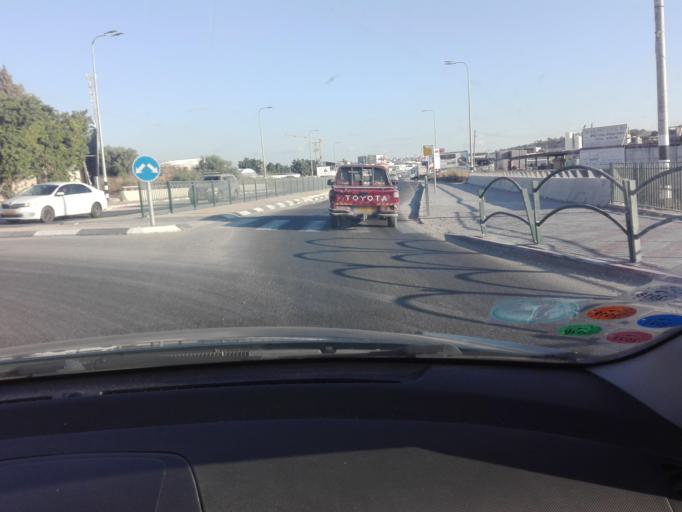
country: PS
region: West Bank
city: Nazlat `Isa
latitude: 32.4026
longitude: 35.0488
